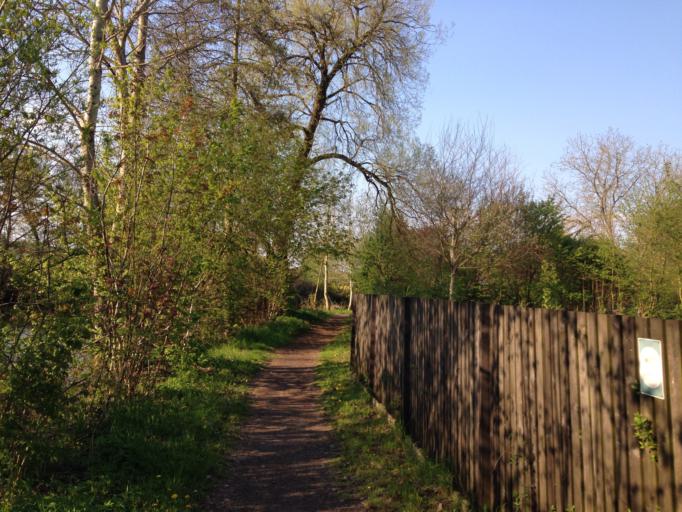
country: DE
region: Hesse
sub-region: Regierungsbezirk Giessen
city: Giessen
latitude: 50.6110
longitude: 8.6672
